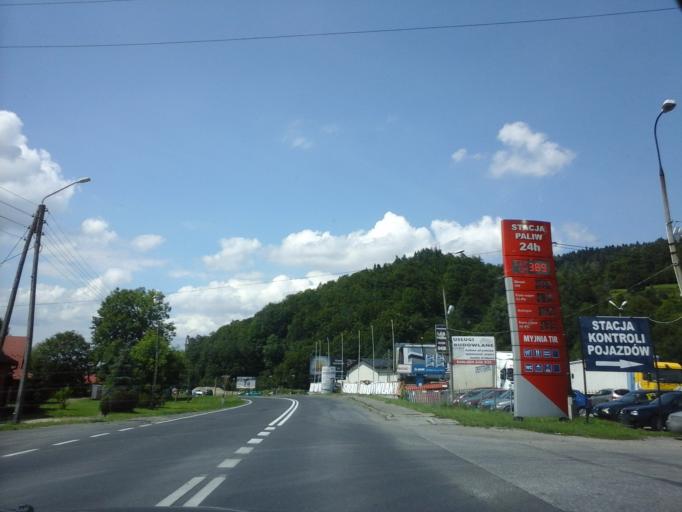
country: PL
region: Lesser Poland Voivodeship
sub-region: Powiat suski
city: Makow Podhalanski
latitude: 49.7322
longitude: 19.6605
